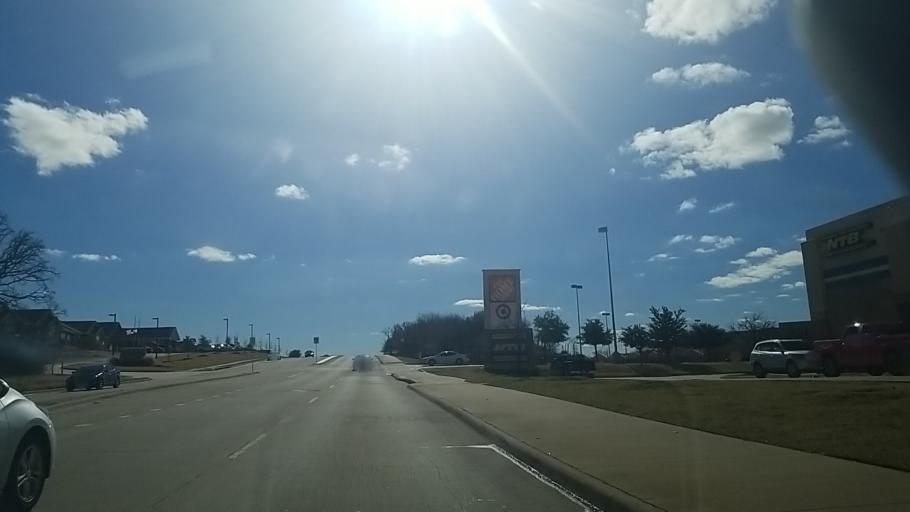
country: US
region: Texas
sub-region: Denton County
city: Denton
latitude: 33.1896
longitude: -97.0959
